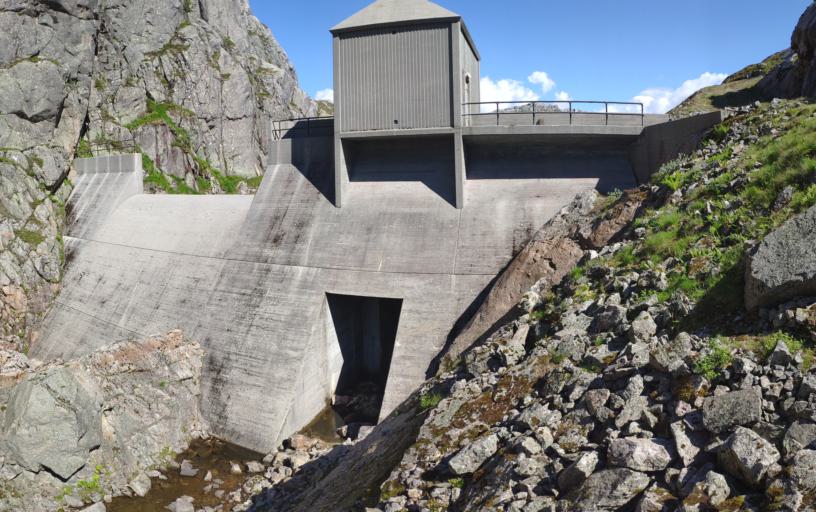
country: NO
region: Vest-Agder
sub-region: Sirdal
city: Tonstad
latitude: 59.0461
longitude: 6.7085
